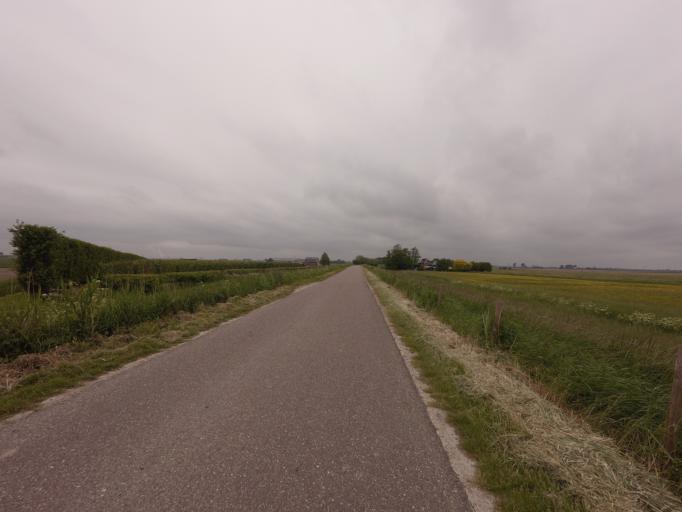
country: NL
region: South Holland
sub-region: Gemeente Spijkenisse
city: Spijkenisse
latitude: 51.7864
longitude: 4.3366
